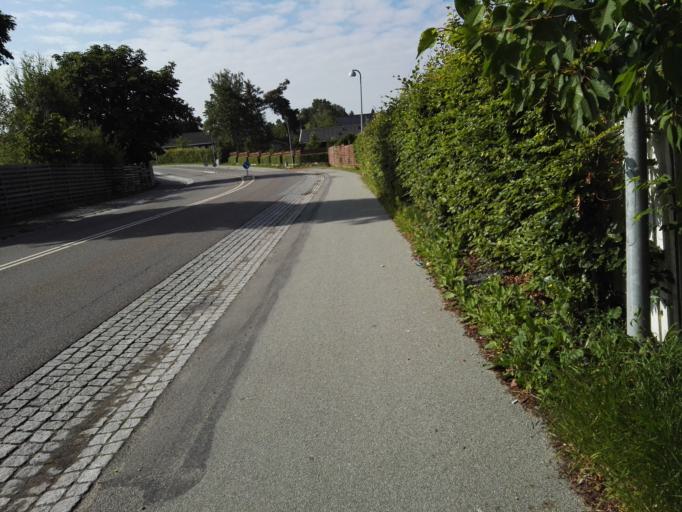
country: DK
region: Zealand
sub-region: Roskilde Kommune
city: Jyllinge
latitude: 55.7680
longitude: 12.1095
